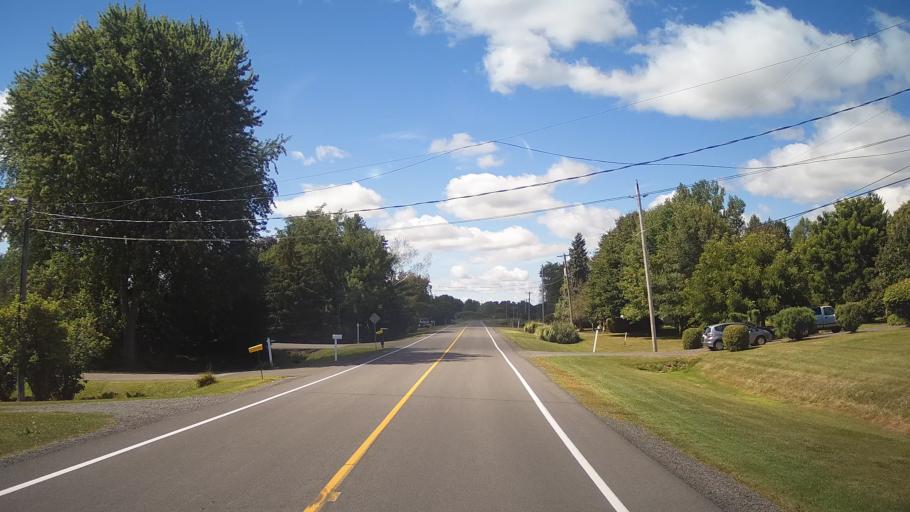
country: US
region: New York
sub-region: St. Lawrence County
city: Ogdensburg
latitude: 44.8597
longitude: -75.2668
